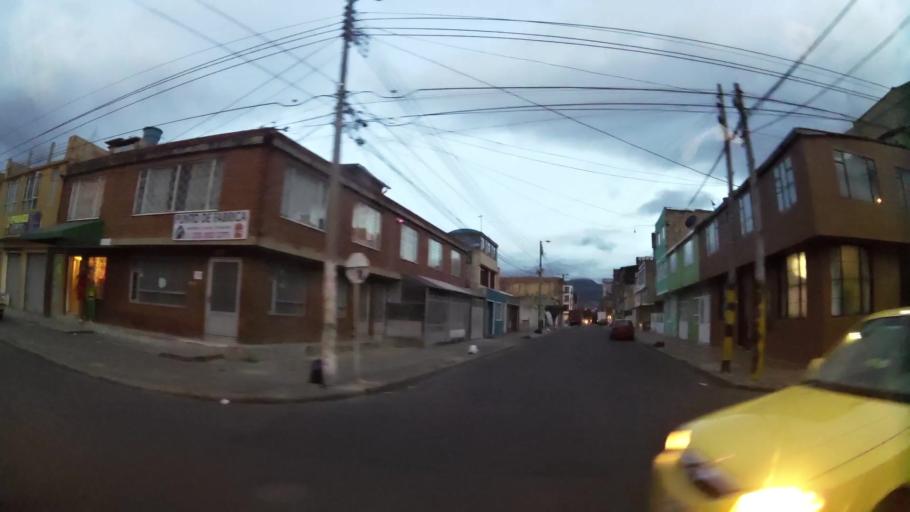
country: CO
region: Bogota D.C.
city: Bogota
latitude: 4.6044
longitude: -74.1302
